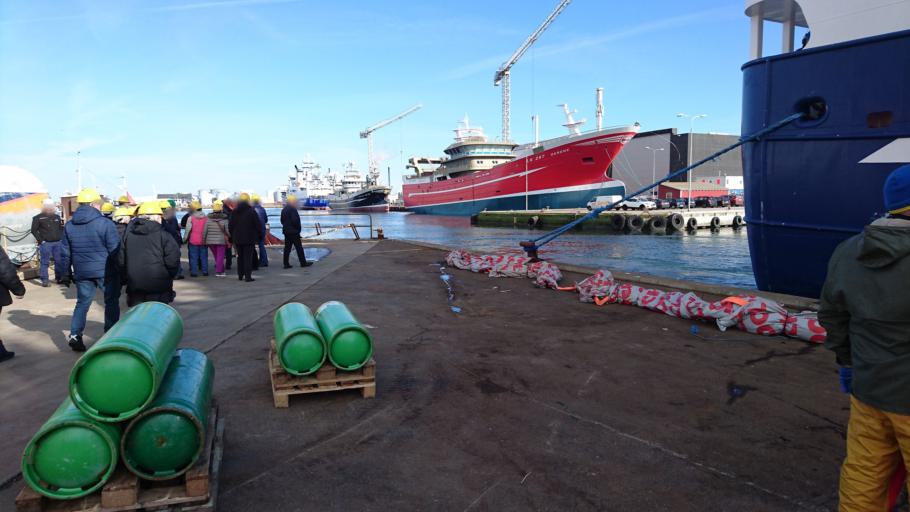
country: DK
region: North Denmark
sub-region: Frederikshavn Kommune
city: Skagen
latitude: 57.7166
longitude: 10.5855
